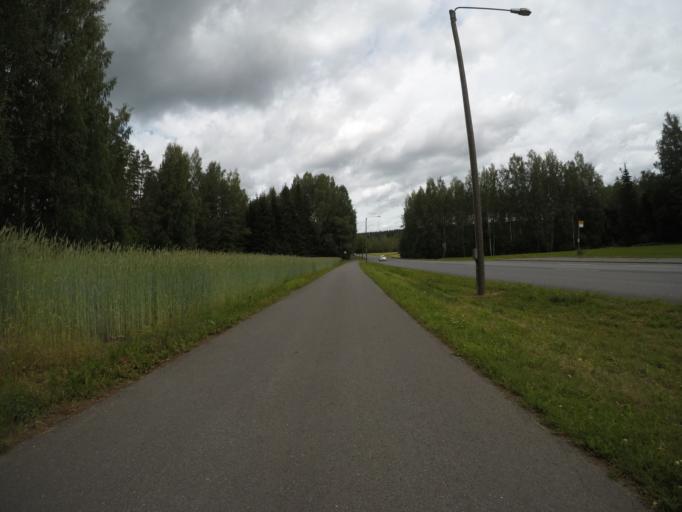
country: FI
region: Haeme
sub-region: Haemeenlinna
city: Haemeenlinna
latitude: 60.9715
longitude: 24.4370
